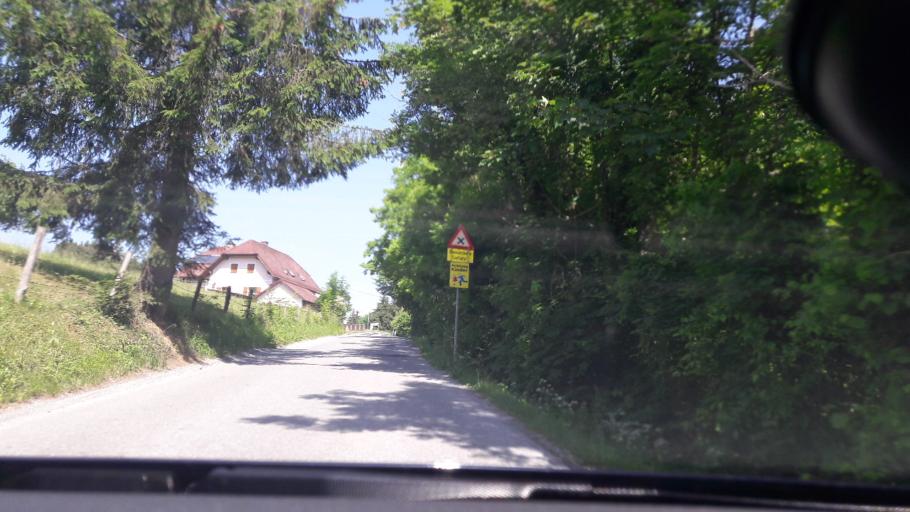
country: AT
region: Styria
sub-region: Politischer Bezirk Voitsberg
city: Sodingberg
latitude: 47.1120
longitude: 15.1500
